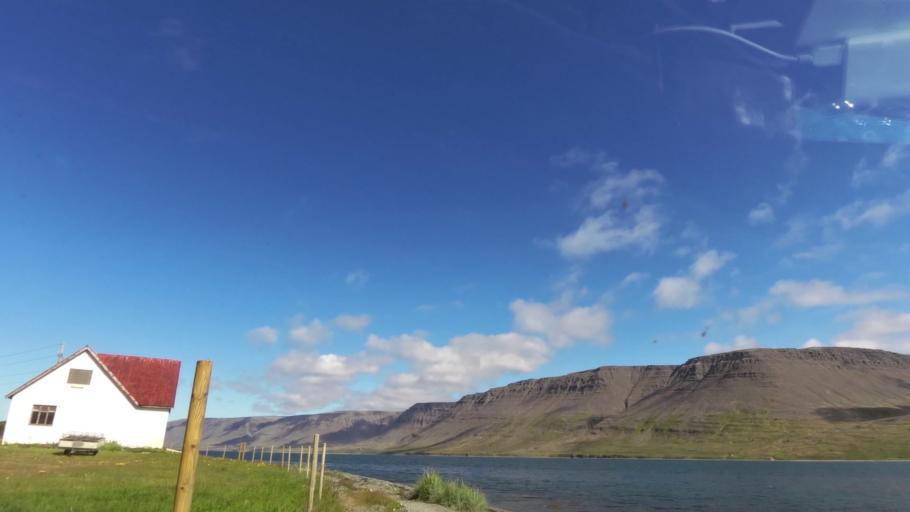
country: IS
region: West
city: Olafsvik
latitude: 65.6218
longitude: -23.8688
